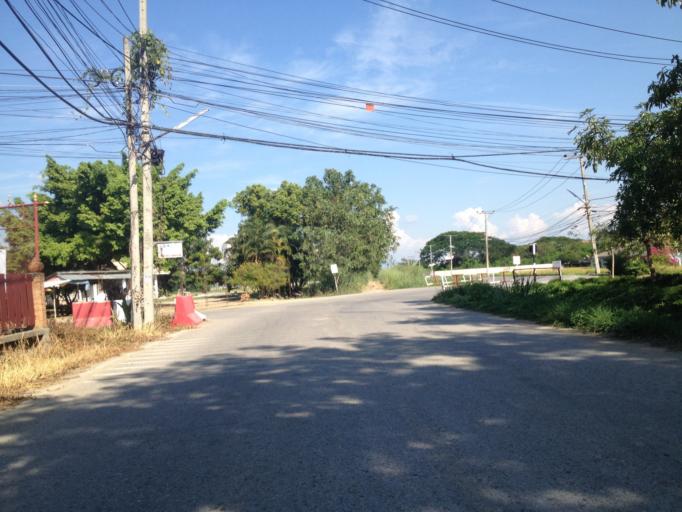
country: TH
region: Chiang Mai
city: Chiang Mai
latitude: 18.7336
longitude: 98.9606
